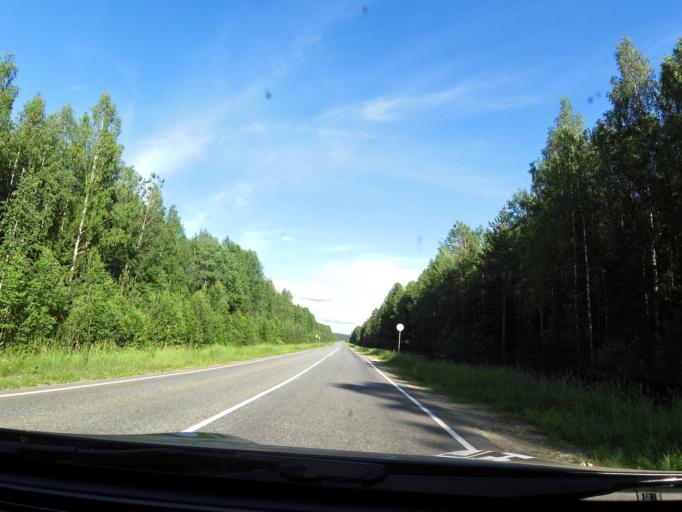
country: RU
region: Kirov
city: Chernaya Kholunitsa
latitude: 58.8297
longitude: 51.7639
